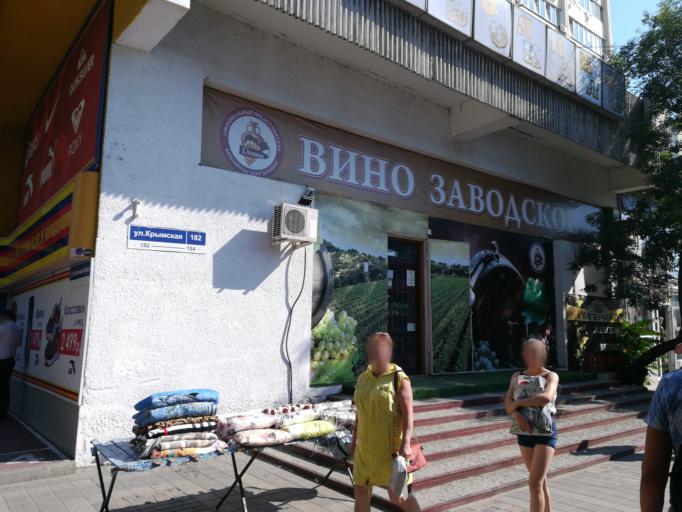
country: RU
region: Krasnodarskiy
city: Anapa
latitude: 44.8974
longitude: 37.3239
